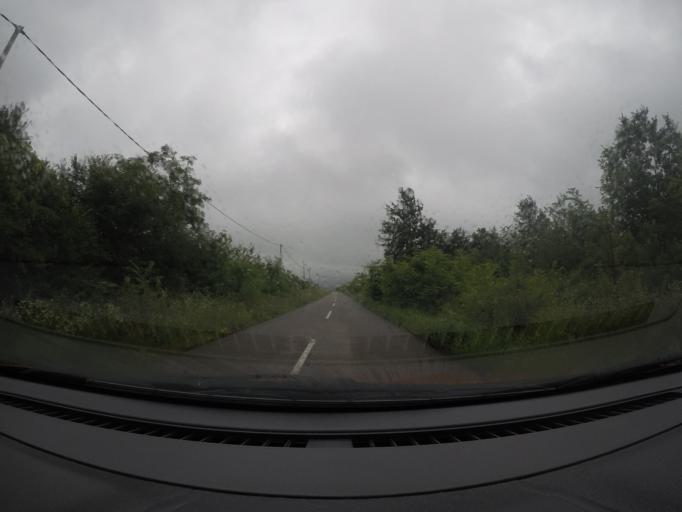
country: RS
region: Central Serbia
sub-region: Belgrade
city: Sopot
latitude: 44.5176
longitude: 20.5359
